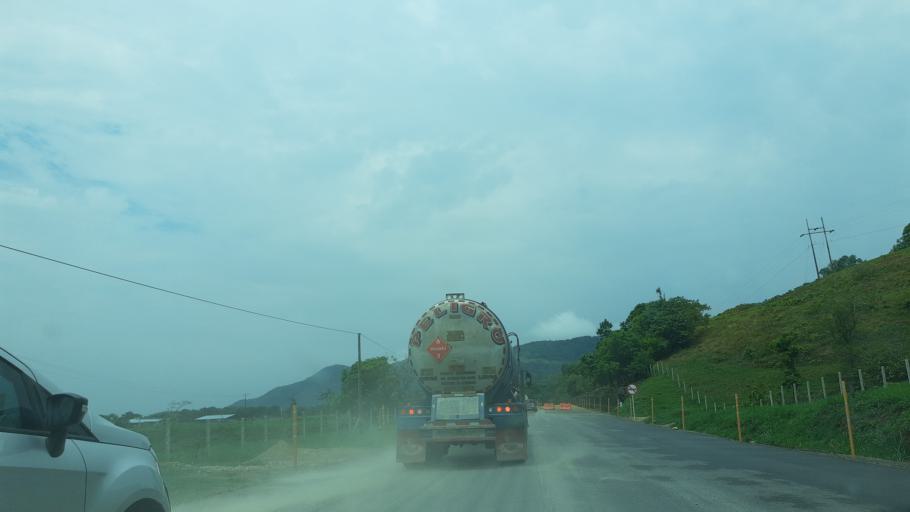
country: CO
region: Casanare
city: Sabanalarga
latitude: 4.7833
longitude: -72.9979
